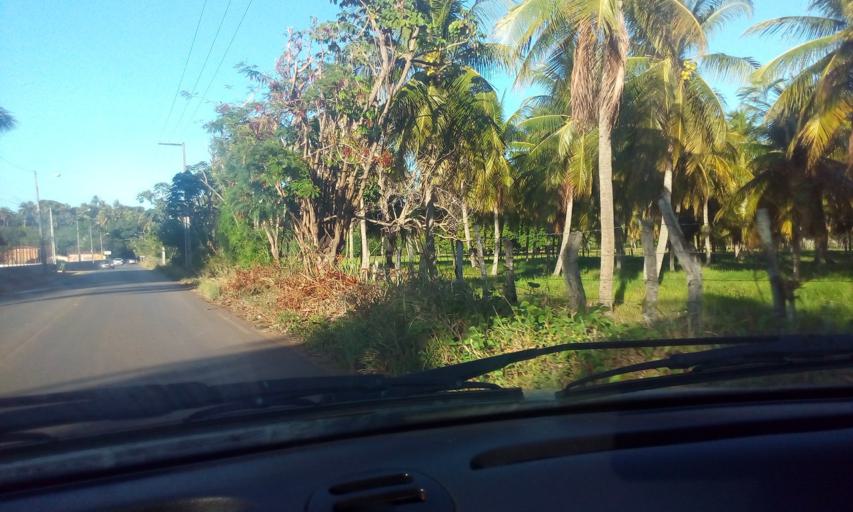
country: BR
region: Rio Grande do Norte
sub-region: Parnamirim
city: Parnamirim
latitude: -5.9558
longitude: -35.1634
